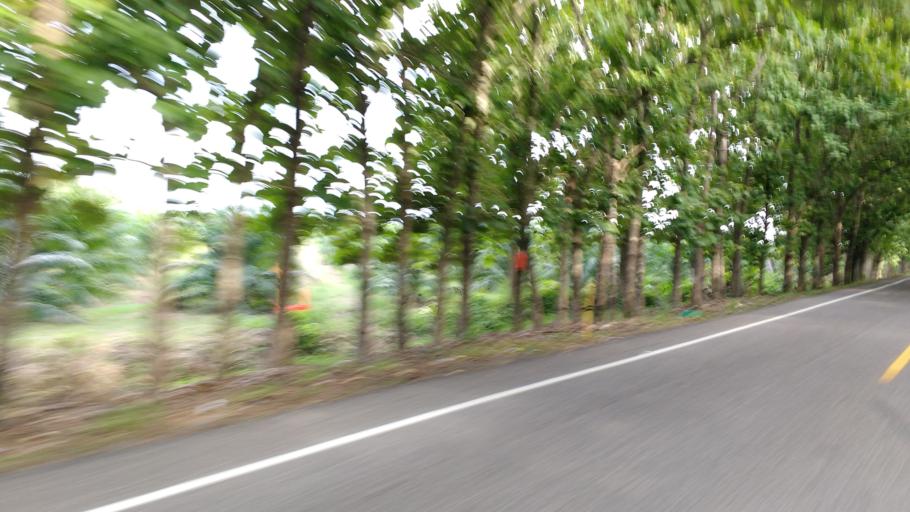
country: MX
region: Tabasco
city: Rio de Teapa
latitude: 17.6831
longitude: -92.9439
